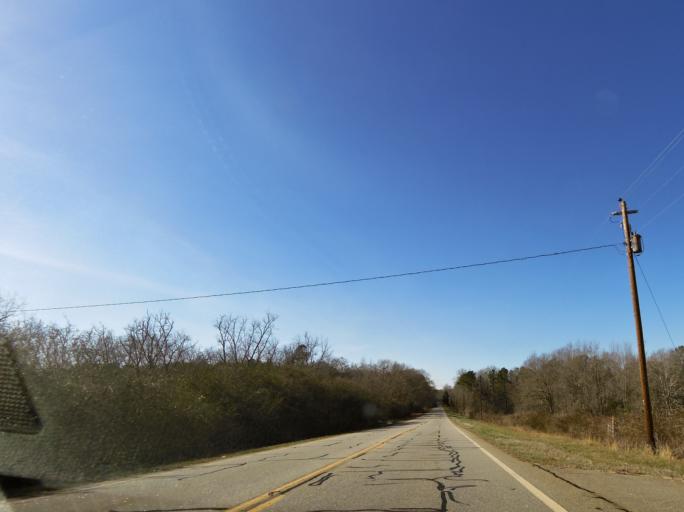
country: US
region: Georgia
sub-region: Lamar County
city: Barnesville
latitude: 32.9148
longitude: -84.1684
